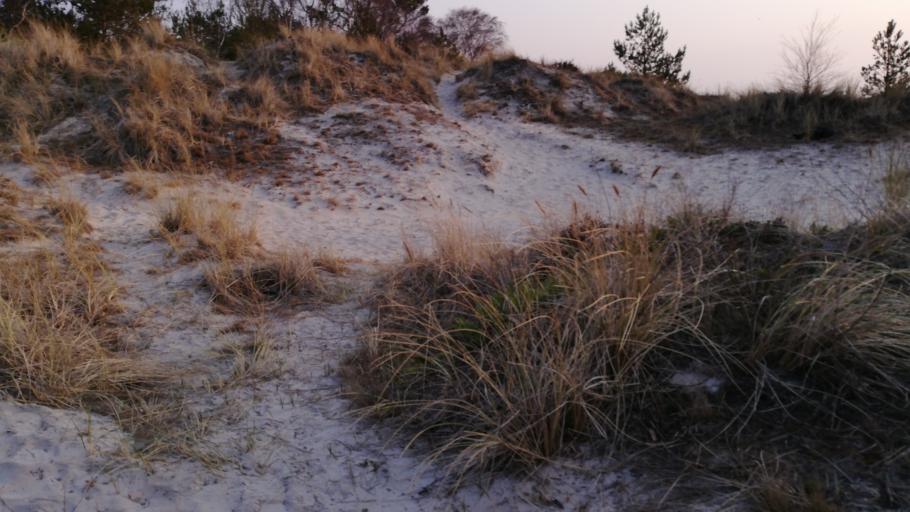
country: SE
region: Skane
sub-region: Simrishamns Kommun
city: Simrishamn
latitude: 55.3849
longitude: 14.1956
